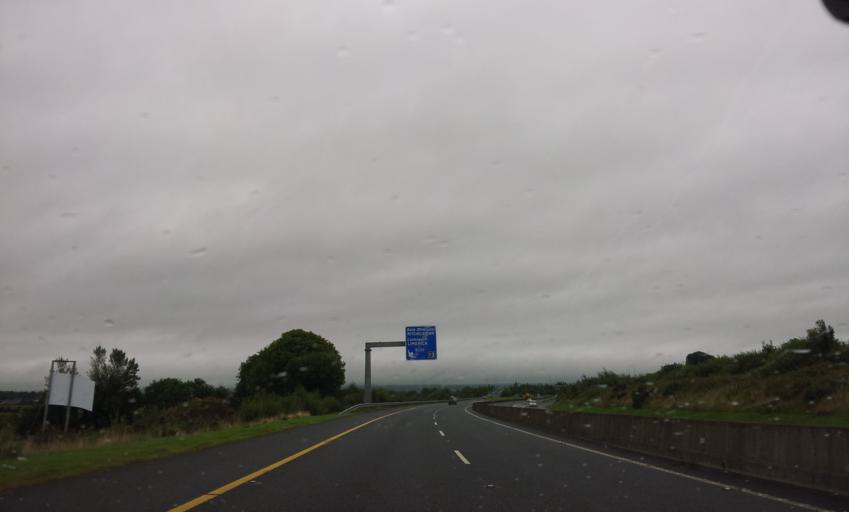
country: IE
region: Munster
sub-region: County Cork
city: Mitchelstown
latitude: 52.2332
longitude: -8.2856
